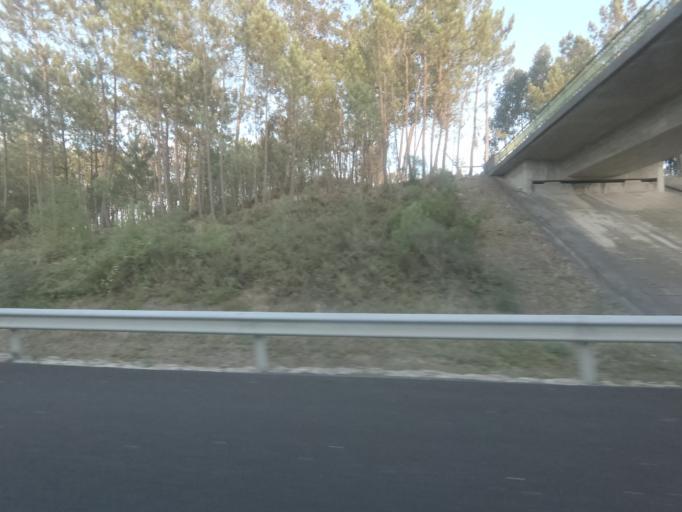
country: PT
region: Leiria
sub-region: Leiria
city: Caranguejeira
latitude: 39.8025
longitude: -8.7249
